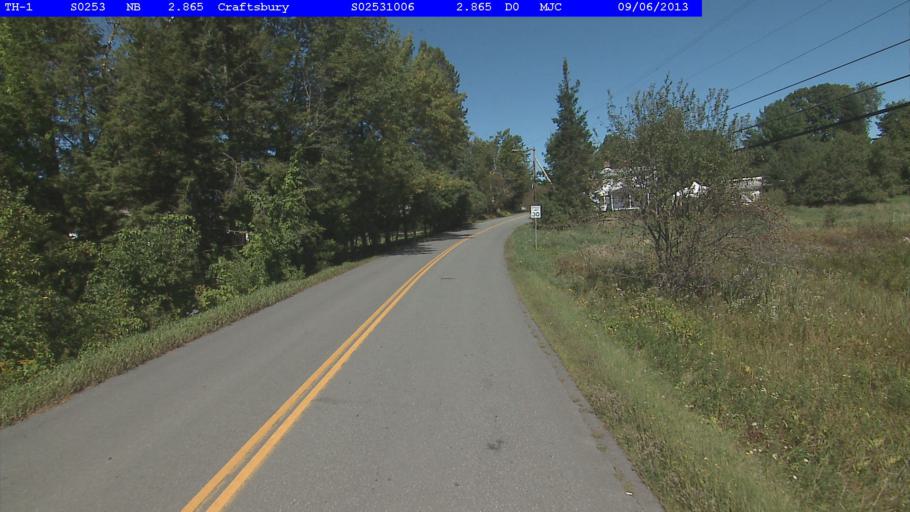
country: US
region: Vermont
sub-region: Caledonia County
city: Hardwick
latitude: 44.6495
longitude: -72.3812
